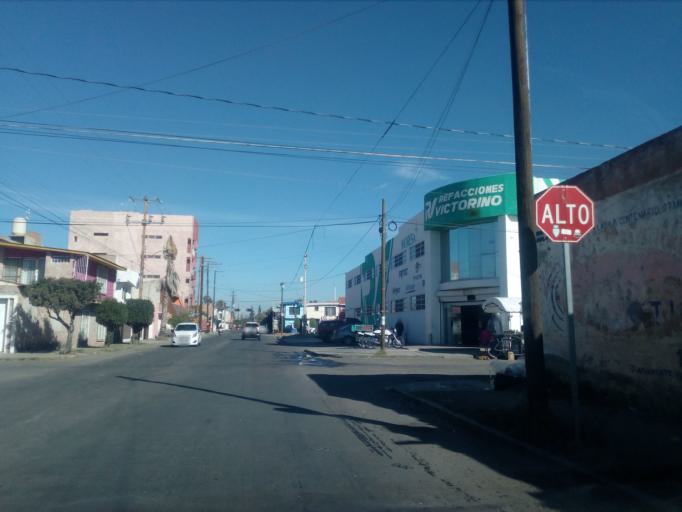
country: MX
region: Durango
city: Victoria de Durango
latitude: 24.0313
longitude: -104.6346
